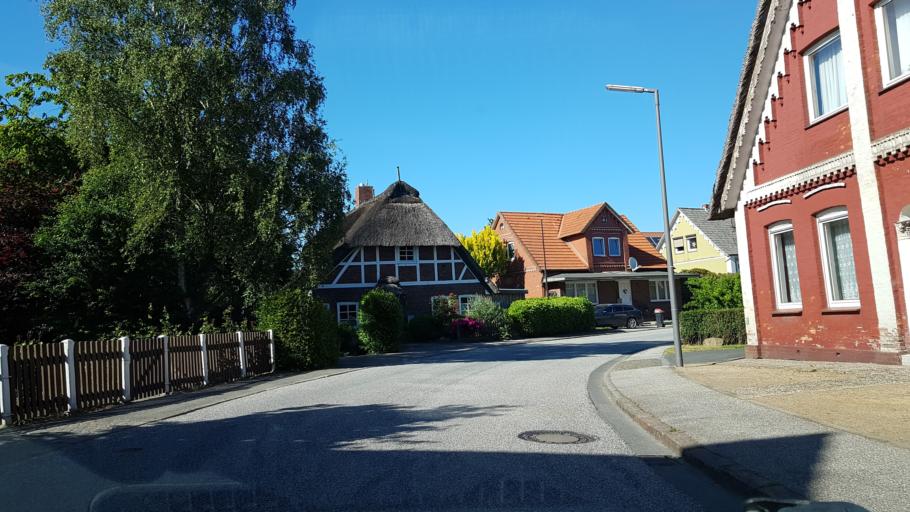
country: DE
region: Lower Saxony
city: Neu Wulmstorf
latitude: 53.5211
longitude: 9.7998
